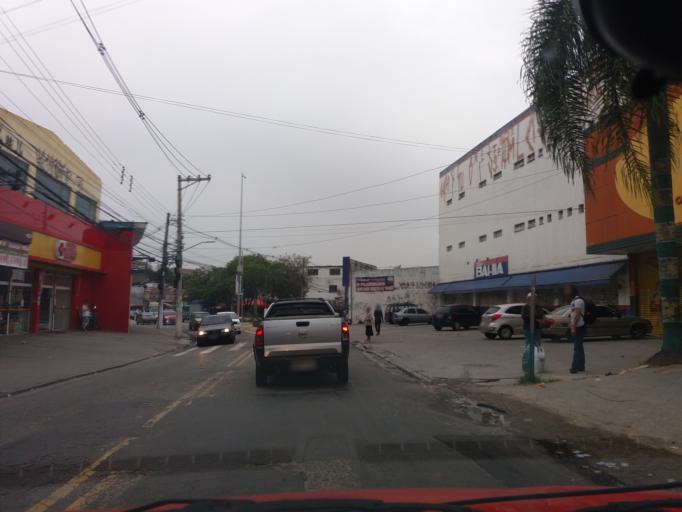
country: BR
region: Sao Paulo
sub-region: Osasco
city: Osasco
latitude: -23.5026
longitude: -46.7906
